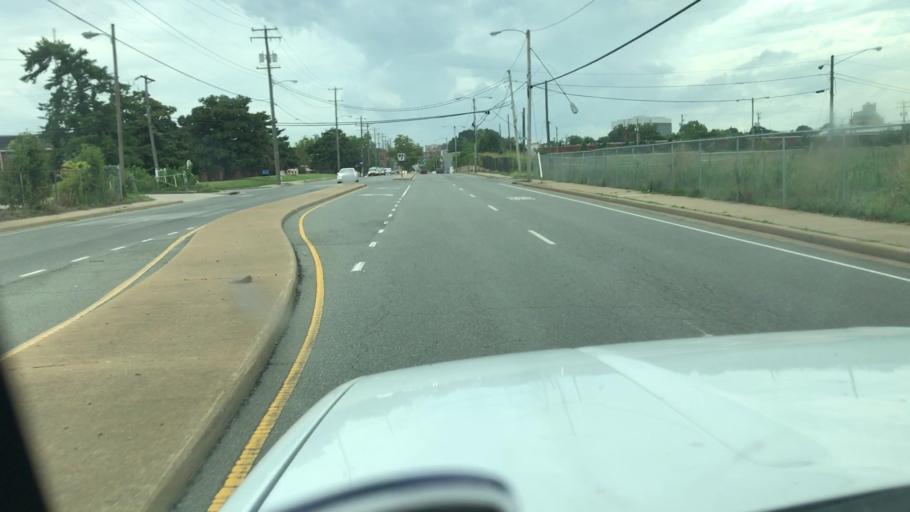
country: US
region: Virginia
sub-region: City of Richmond
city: Richmond
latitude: 37.5697
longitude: -77.4608
